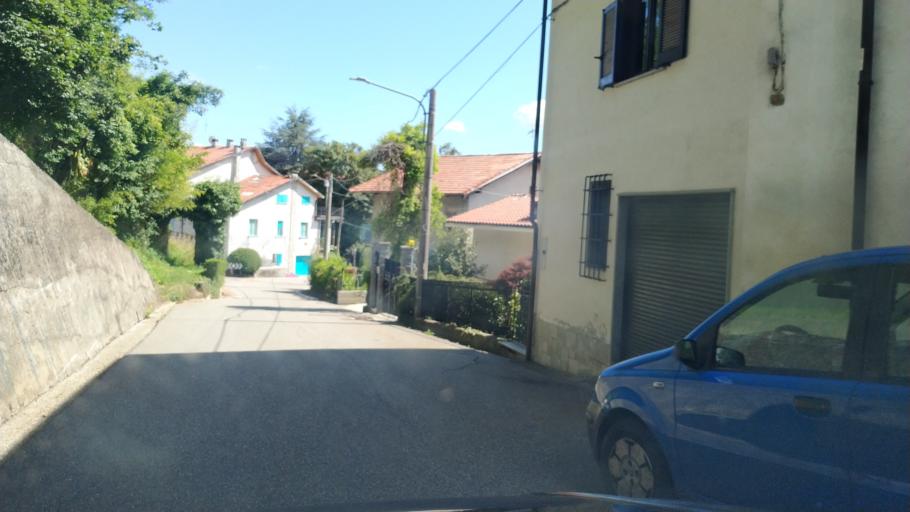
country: IT
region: Piedmont
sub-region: Provincia di Torino
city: Castelnuovo Nigra
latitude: 45.4287
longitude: 7.7035
